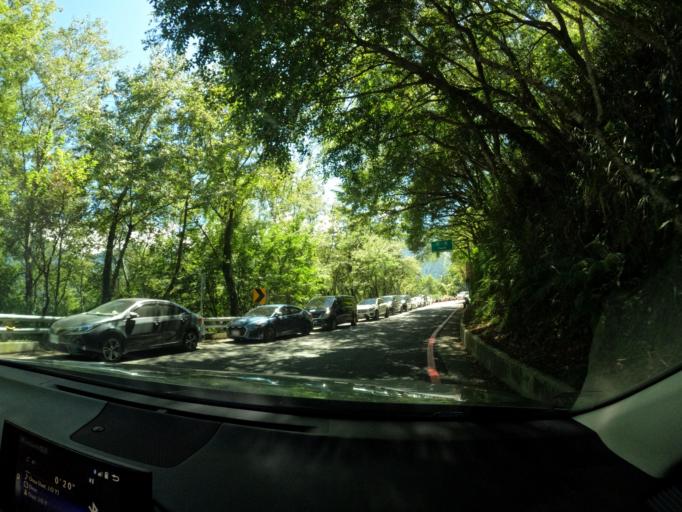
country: TW
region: Taiwan
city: Yujing
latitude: 23.2779
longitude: 120.9172
